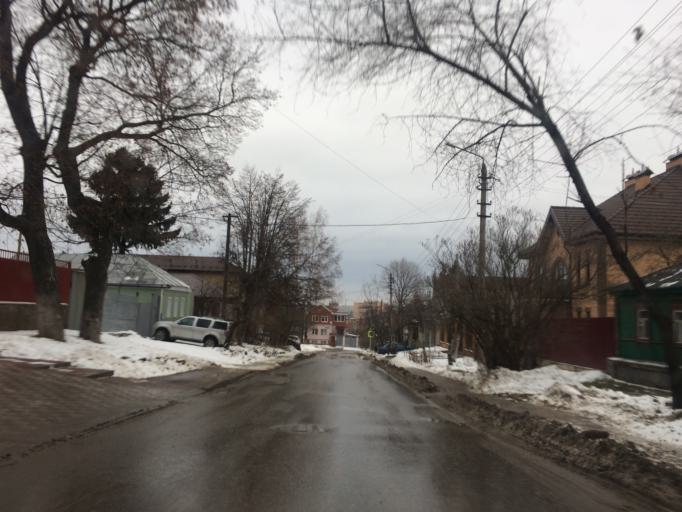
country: RU
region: Tula
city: Tula
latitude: 54.1810
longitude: 37.6178
